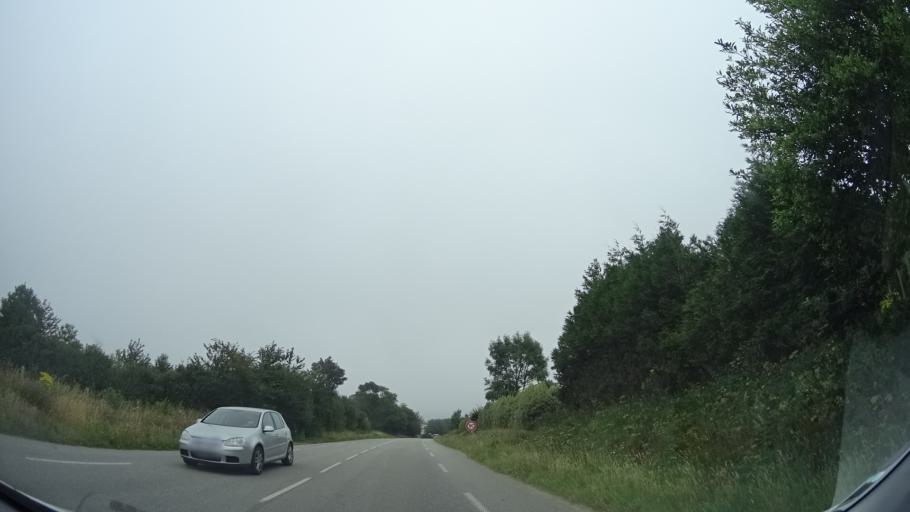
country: FR
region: Lower Normandy
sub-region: Departement de la Manche
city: Les Pieux
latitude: 49.5175
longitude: -1.8048
